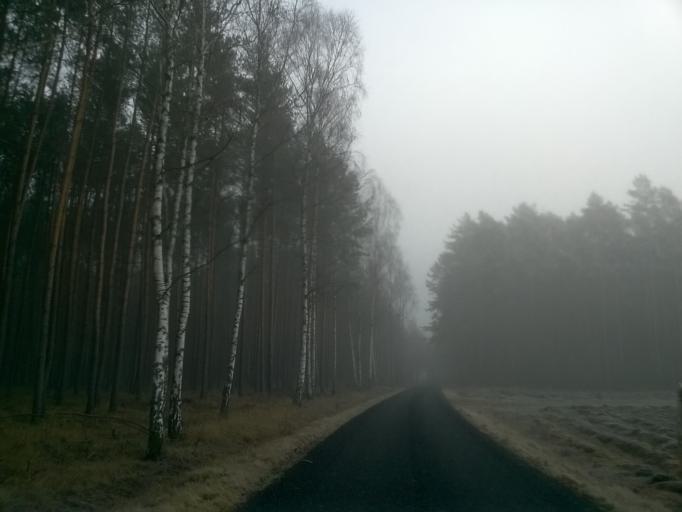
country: PL
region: Kujawsko-Pomorskie
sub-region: Powiat nakielski
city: Kcynia
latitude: 53.0539
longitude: 17.4222
